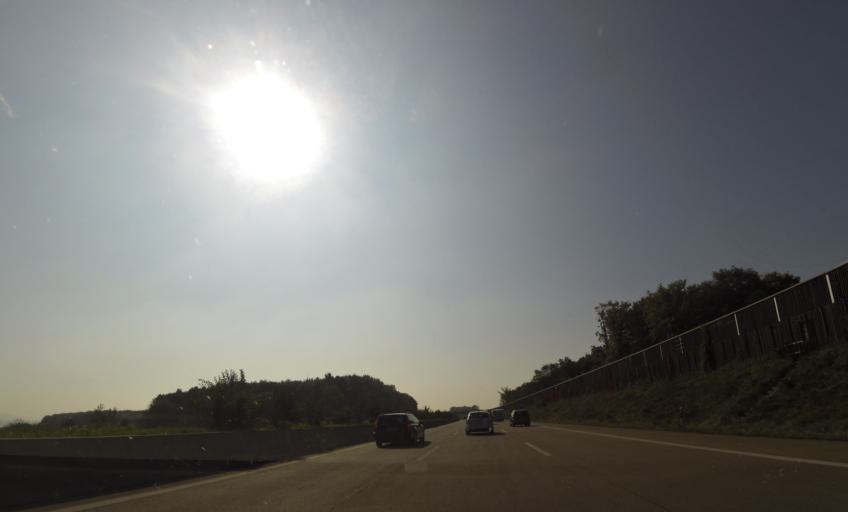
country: DE
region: Baden-Wuerttemberg
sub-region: Karlsruhe Region
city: Zell
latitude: 48.6634
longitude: 8.0414
